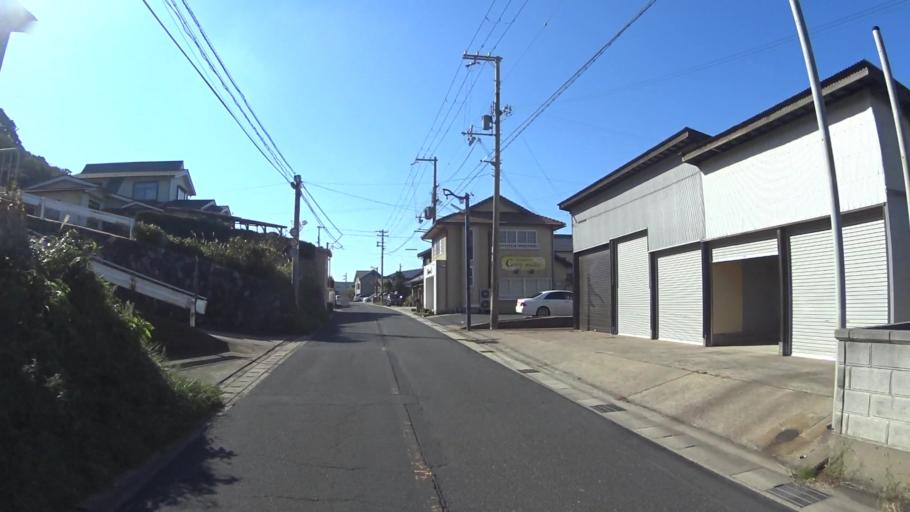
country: JP
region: Kyoto
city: Miyazu
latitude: 35.7398
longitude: 135.0986
